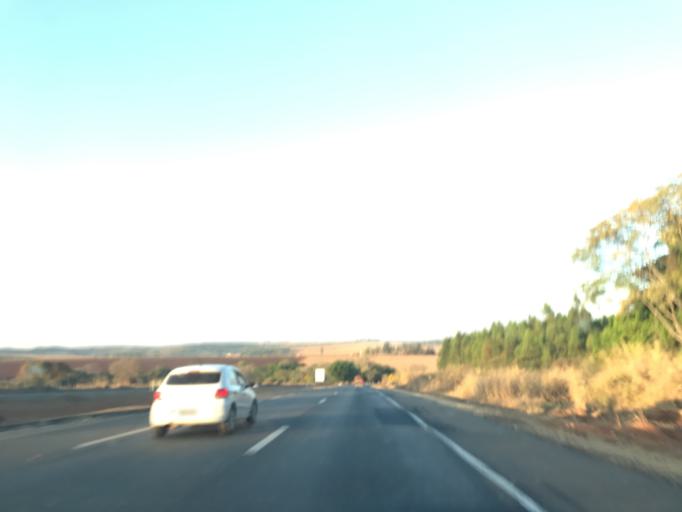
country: BR
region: Goias
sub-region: Abadiania
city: Abadiania
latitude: -16.2810
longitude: -48.7917
